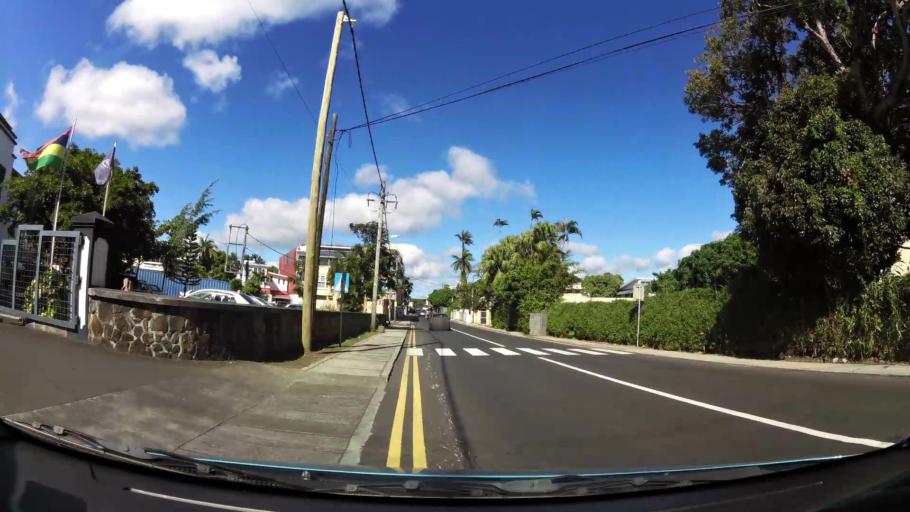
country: MU
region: Plaines Wilhems
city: Vacoas
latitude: -20.3018
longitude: 57.4926
